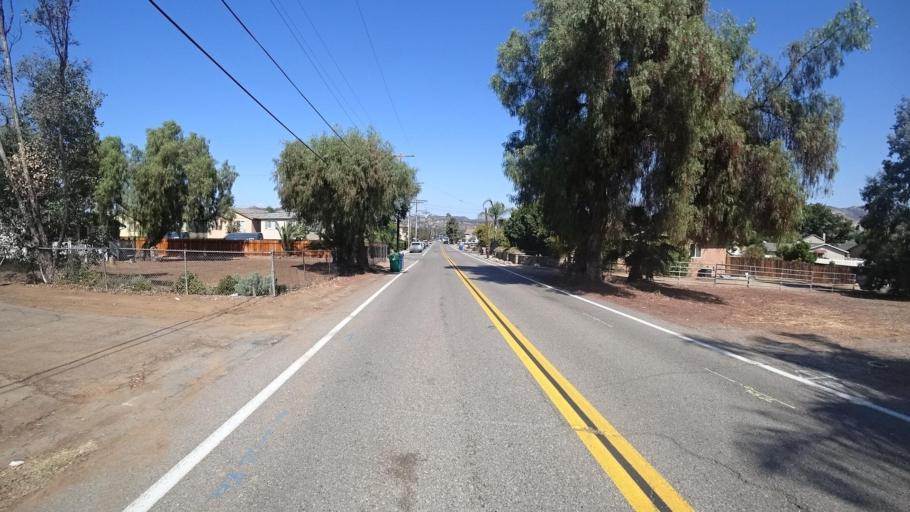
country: US
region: California
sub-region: San Diego County
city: Lakeside
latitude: 32.8524
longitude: -116.9359
